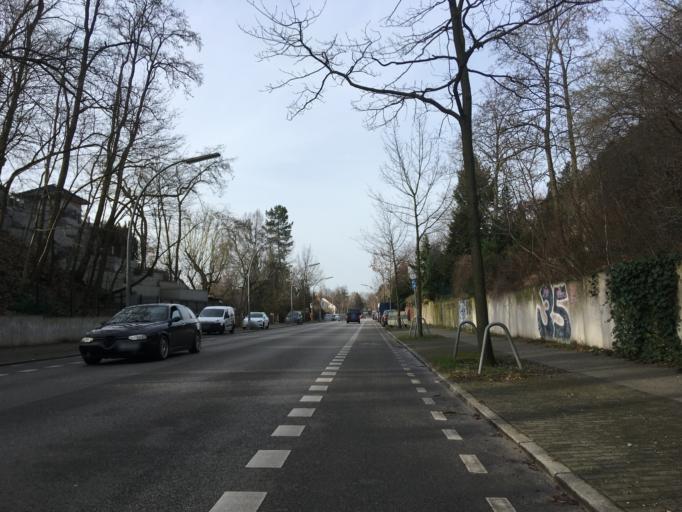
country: DE
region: Berlin
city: Lubars
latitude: 52.6141
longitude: 13.3568
